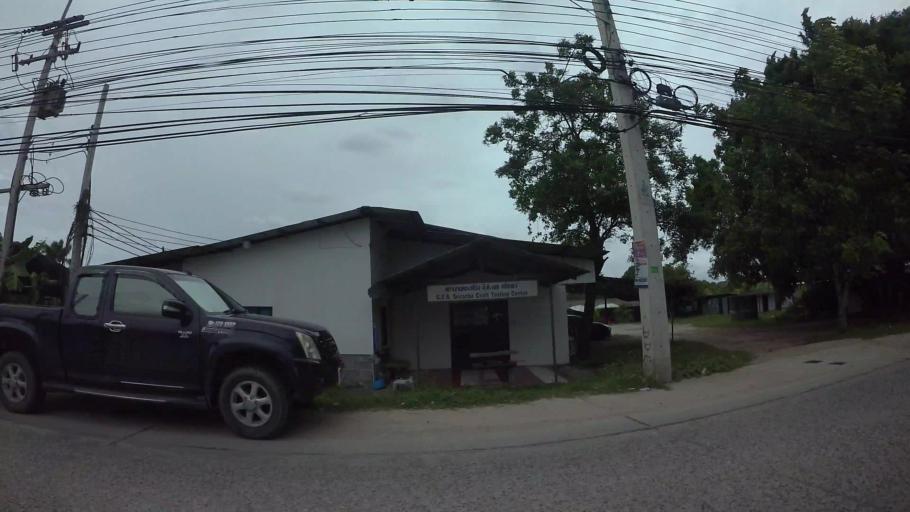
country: TH
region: Chon Buri
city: Si Racha
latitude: 13.1597
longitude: 100.9697
